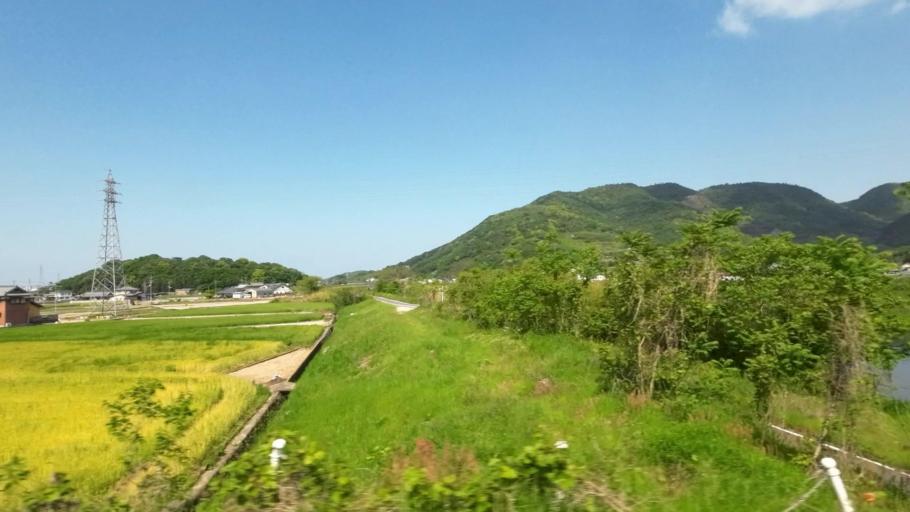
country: JP
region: Kagawa
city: Kan'onjicho
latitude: 34.1385
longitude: 133.6848
